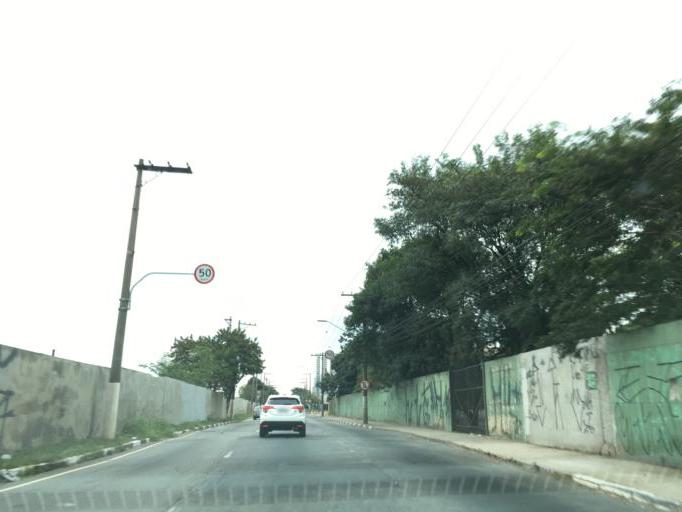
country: BR
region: Sao Paulo
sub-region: Osasco
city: Osasco
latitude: -23.5412
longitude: -46.7374
